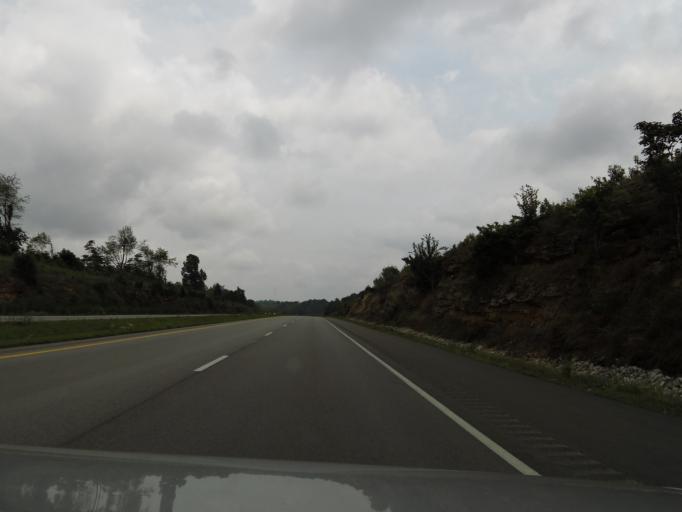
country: US
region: Kentucky
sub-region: Grayson County
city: Leitchfield
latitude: 37.4511
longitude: -86.3310
